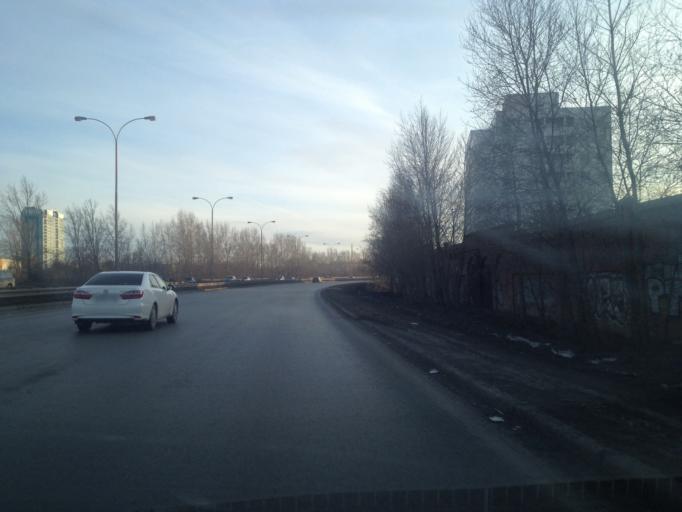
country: RU
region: Sverdlovsk
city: Yekaterinburg
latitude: 56.7902
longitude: 60.6369
